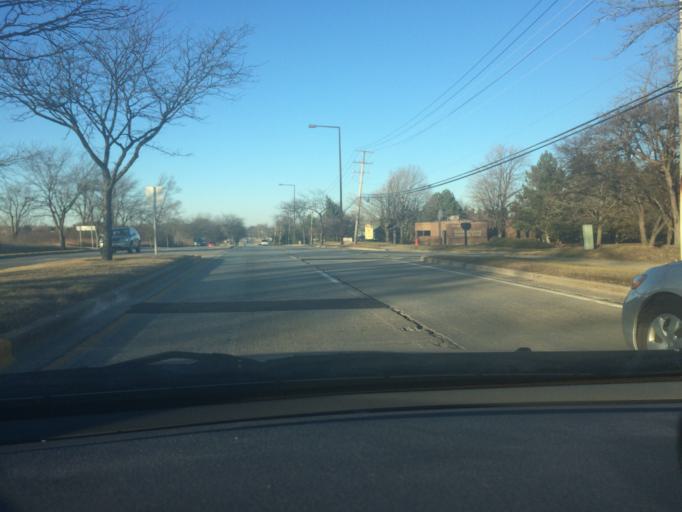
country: US
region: Illinois
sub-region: Cook County
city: Buffalo Grove
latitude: 42.1551
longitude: -87.9849
